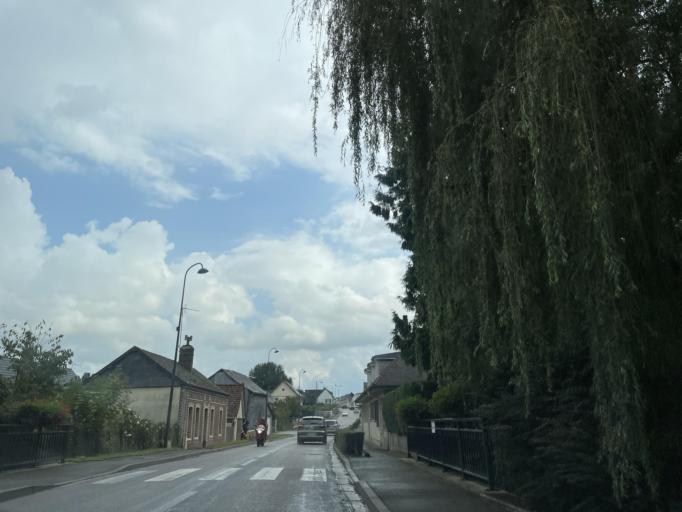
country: FR
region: Haute-Normandie
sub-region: Departement de la Seine-Maritime
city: Envermeu
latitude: 49.8913
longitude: 1.2757
